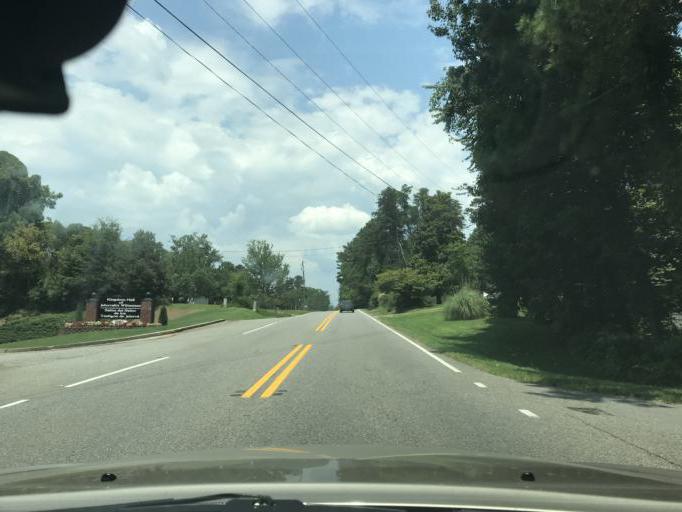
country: US
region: Georgia
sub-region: Forsyth County
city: Cumming
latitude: 34.2389
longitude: -84.1702
